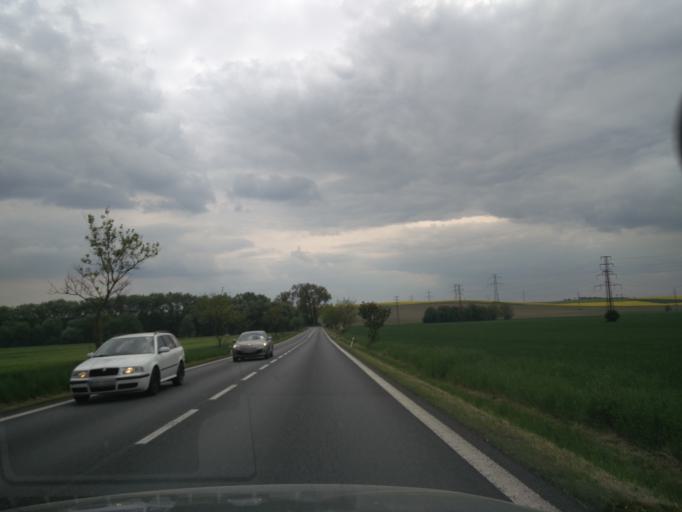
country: CZ
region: Jihocesky
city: Mirovice
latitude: 49.5629
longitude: 14.0785
